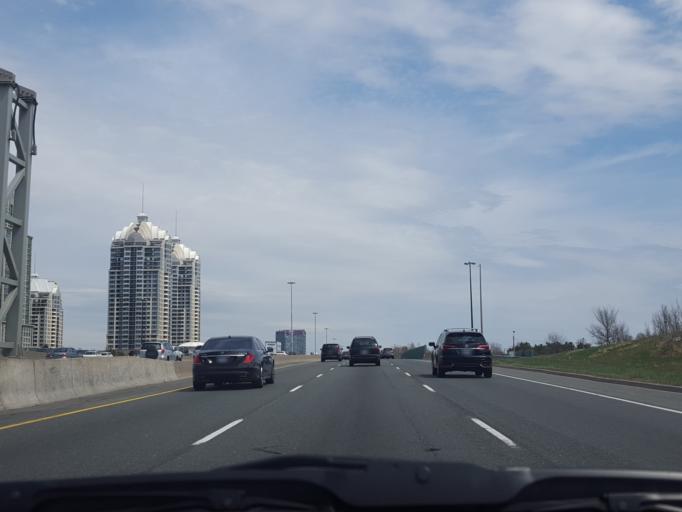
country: CA
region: Ontario
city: Willowdale
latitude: 43.7623
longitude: -79.3894
